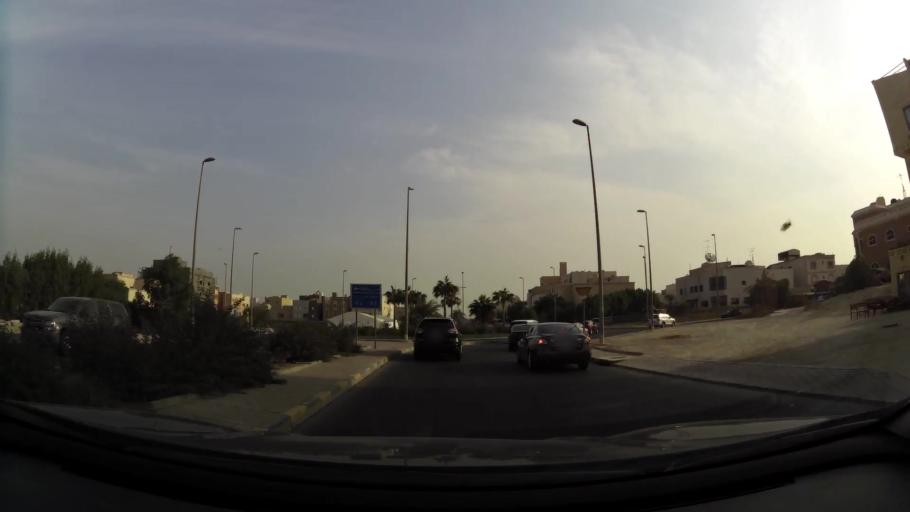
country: KW
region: Mubarak al Kabir
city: Mubarak al Kabir
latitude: 29.1911
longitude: 48.0702
